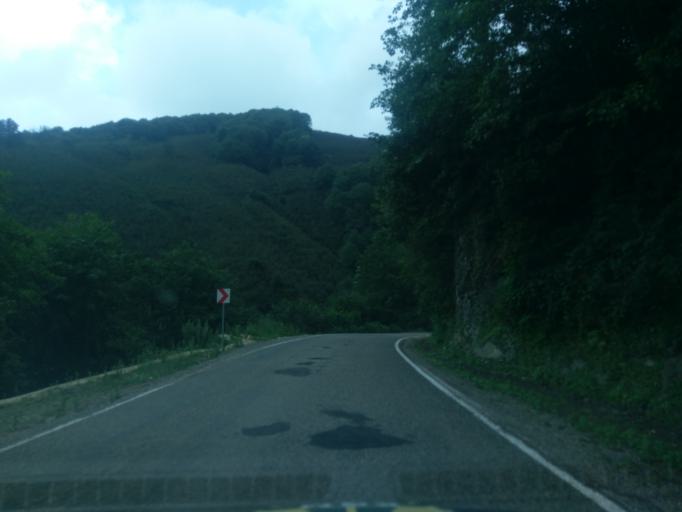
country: TR
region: Ordu
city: Gurgentepe
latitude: 40.8854
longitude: 37.6292
